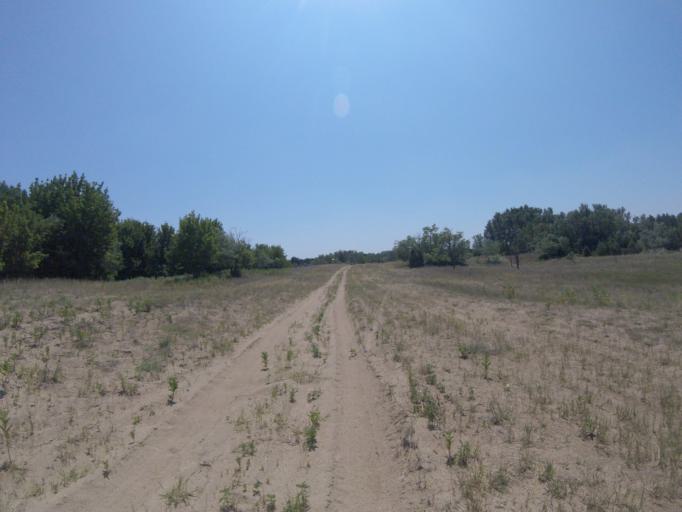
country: HU
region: Bacs-Kiskun
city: Jaszszentlaszlo
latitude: 46.6163
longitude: 19.7104
